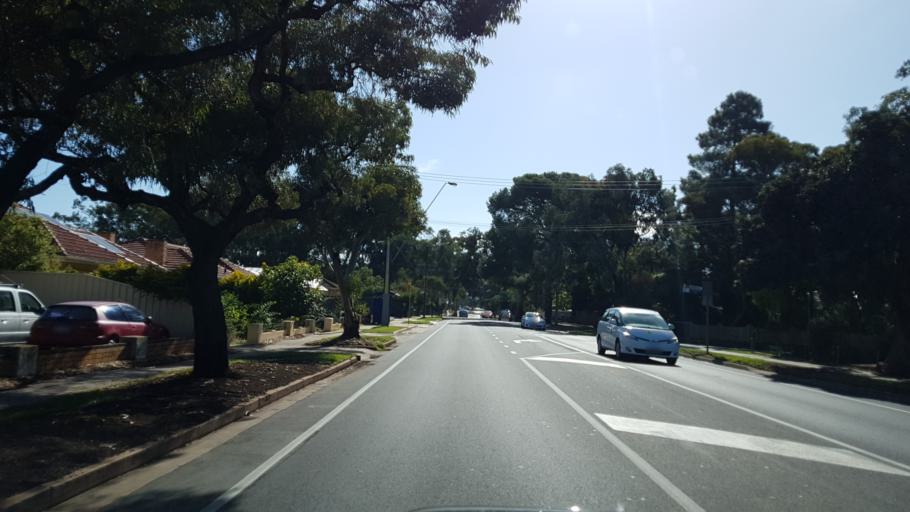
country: AU
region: South Australia
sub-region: Salisbury
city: Salisbury
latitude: -34.7612
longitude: 138.6378
